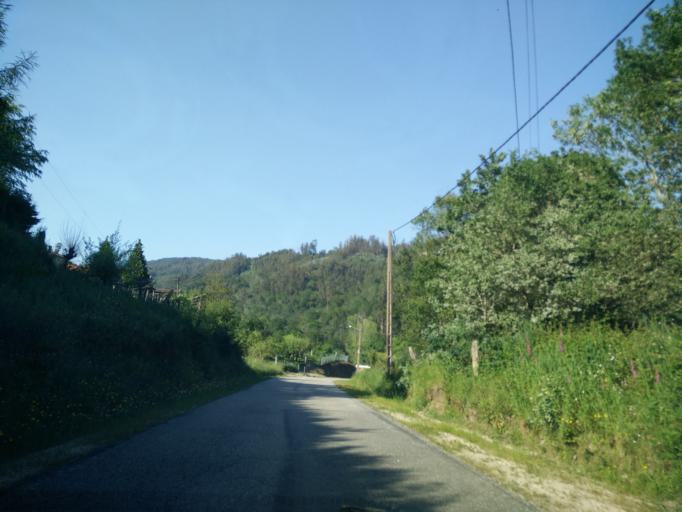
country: ES
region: Galicia
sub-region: Provincia de Pontevedra
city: Mondariz
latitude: 42.2695
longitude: -8.4074
